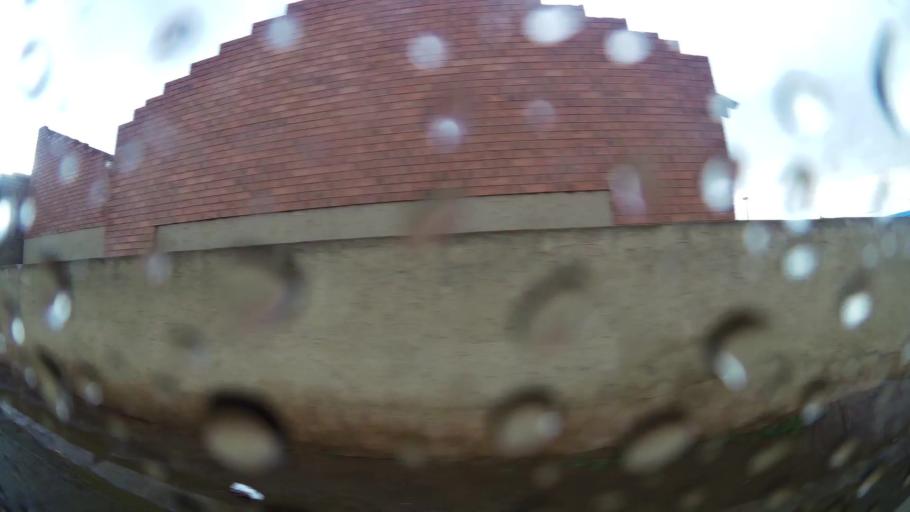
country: ZA
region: Gauteng
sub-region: Ekurhuleni Metropolitan Municipality
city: Germiston
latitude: -26.3718
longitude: 28.1383
